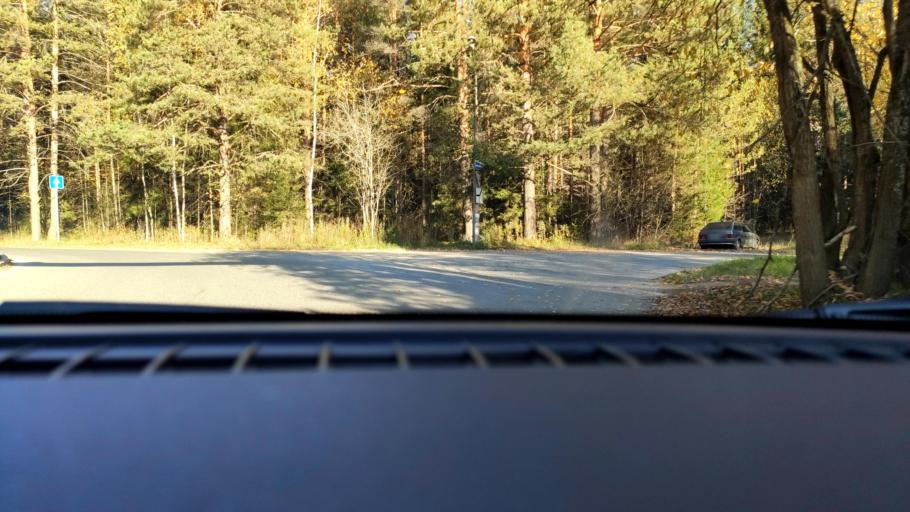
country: RU
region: Perm
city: Perm
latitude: 58.0546
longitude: 56.2301
